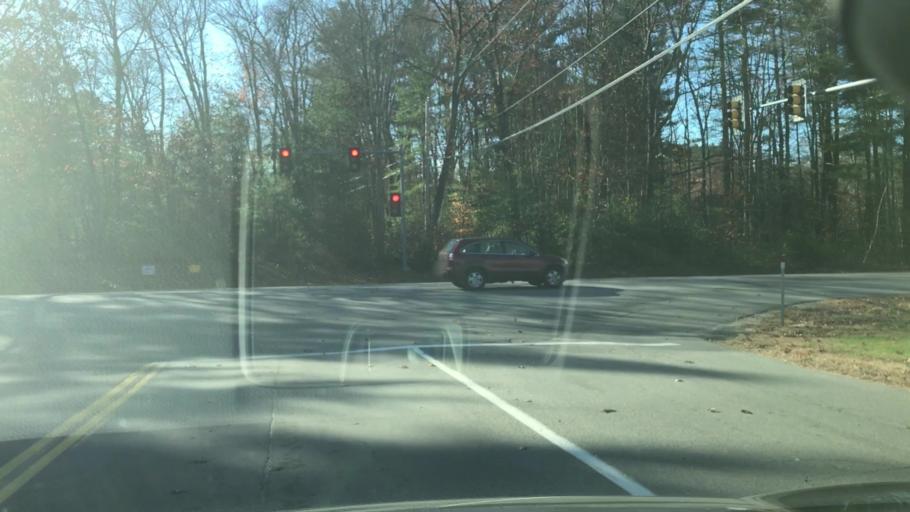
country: US
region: New Hampshire
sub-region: Hillsborough County
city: Pinardville
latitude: 42.9745
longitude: -71.5147
